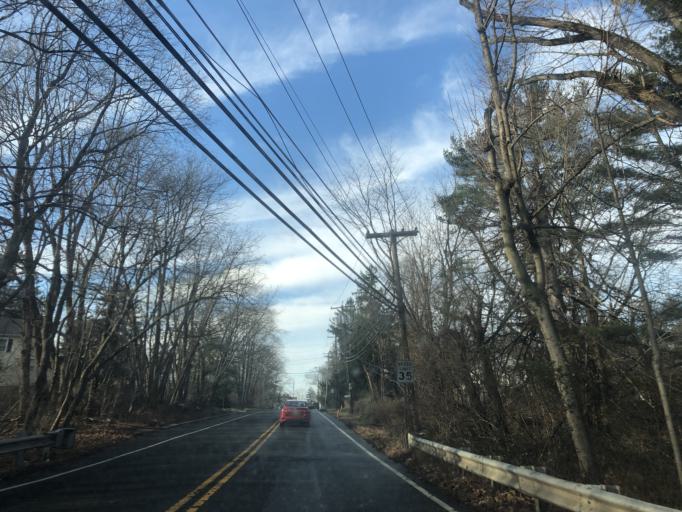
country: US
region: New Jersey
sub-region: Somerset County
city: Kingston
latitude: 40.3773
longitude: -74.6098
